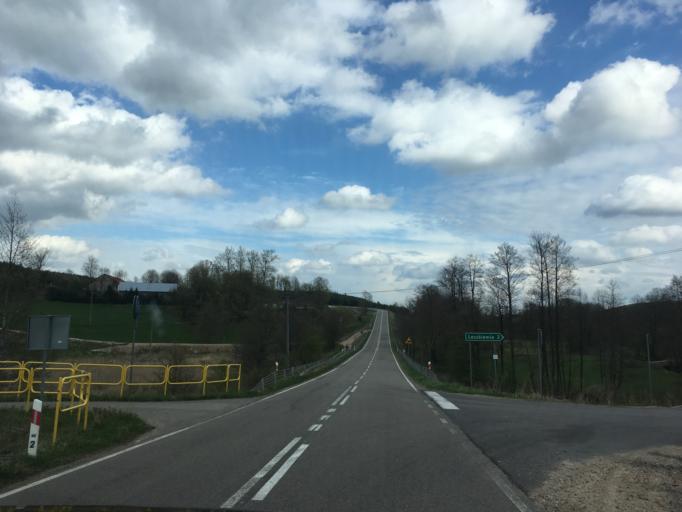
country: PL
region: Podlasie
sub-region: Powiat suwalski
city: Filipow
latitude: 54.3603
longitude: 22.8049
